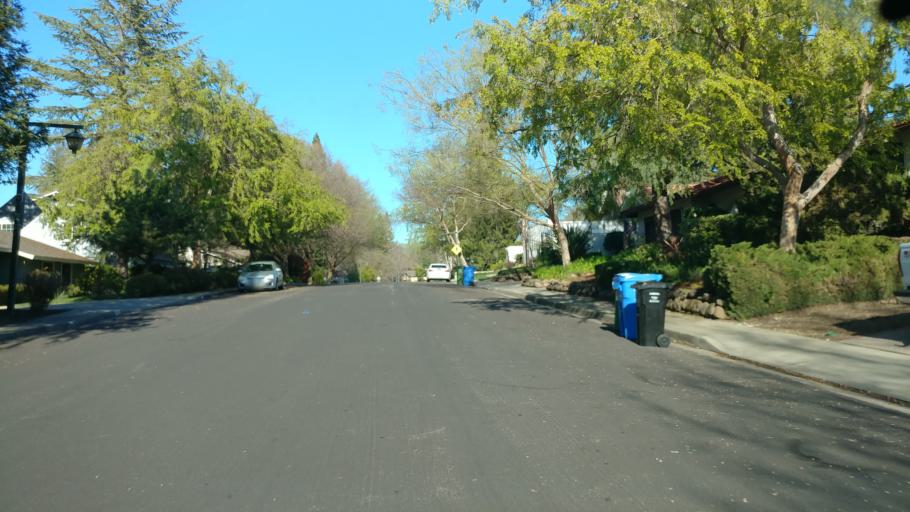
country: US
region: California
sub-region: Contra Costa County
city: Danville
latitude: 37.8147
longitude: -121.9798
